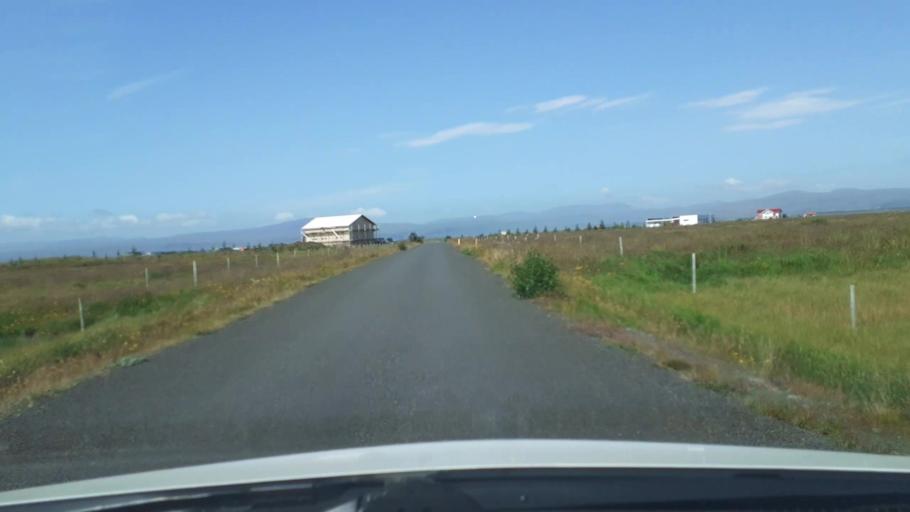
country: IS
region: South
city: Selfoss
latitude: 63.8961
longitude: -21.0808
